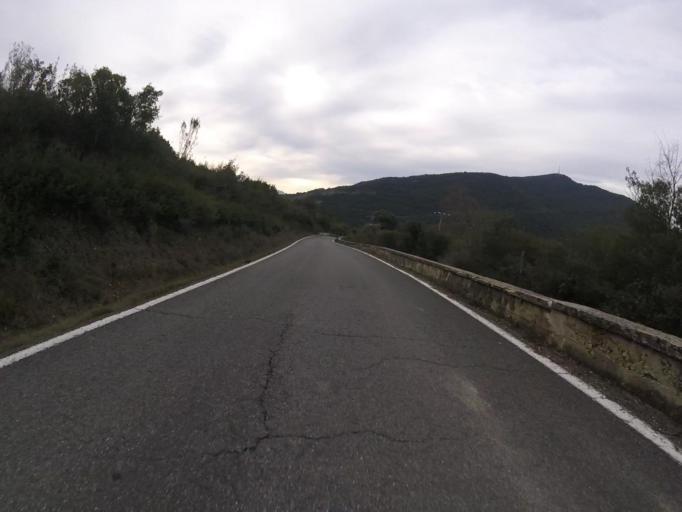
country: ES
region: Navarre
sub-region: Provincia de Navarra
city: Estella
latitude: 42.7000
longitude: -2.0537
